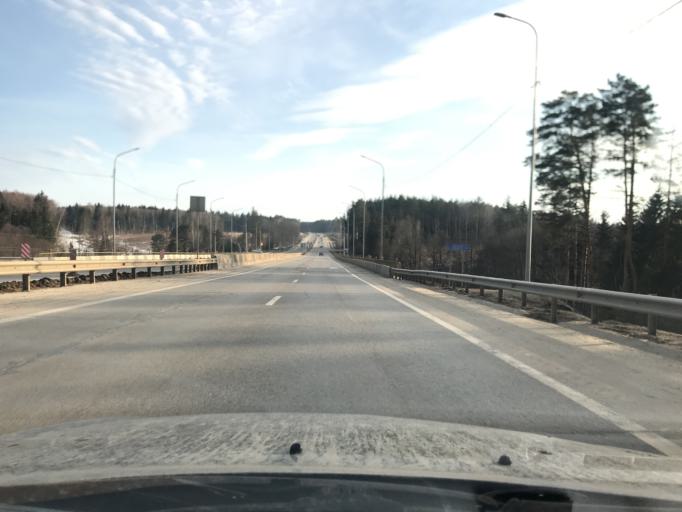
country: RU
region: Kaluga
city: Kaluga
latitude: 54.4253
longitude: 36.2064
